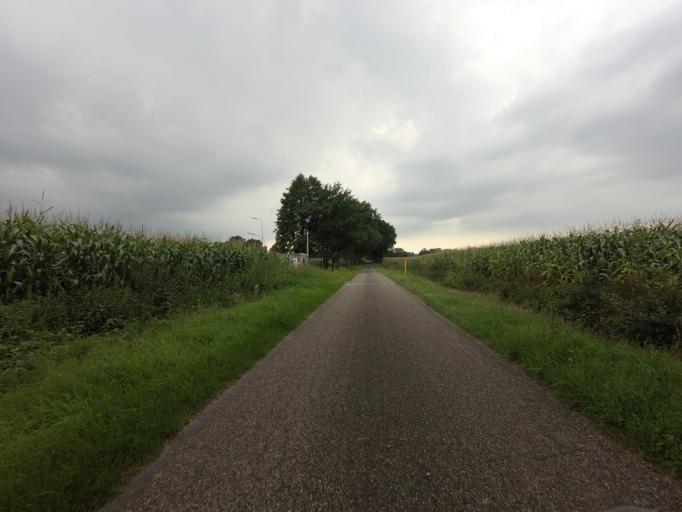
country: DE
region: Lower Saxony
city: Uelsen
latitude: 52.4556
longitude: 6.8954
